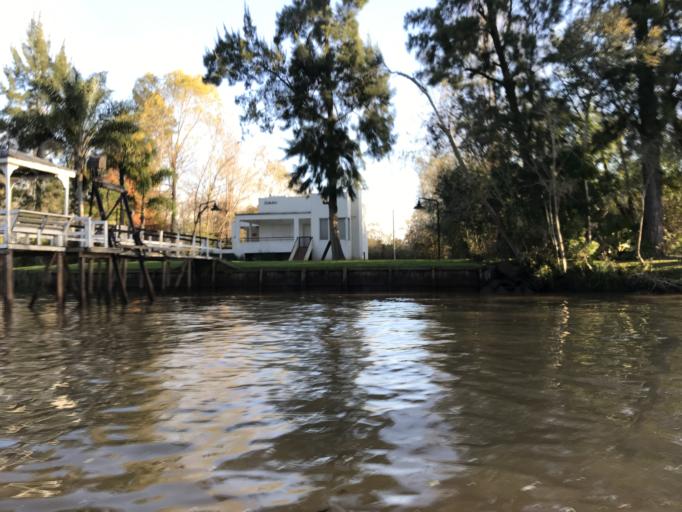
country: AR
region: Buenos Aires
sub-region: Partido de Tigre
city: Tigre
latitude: -34.3764
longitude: -58.5770
